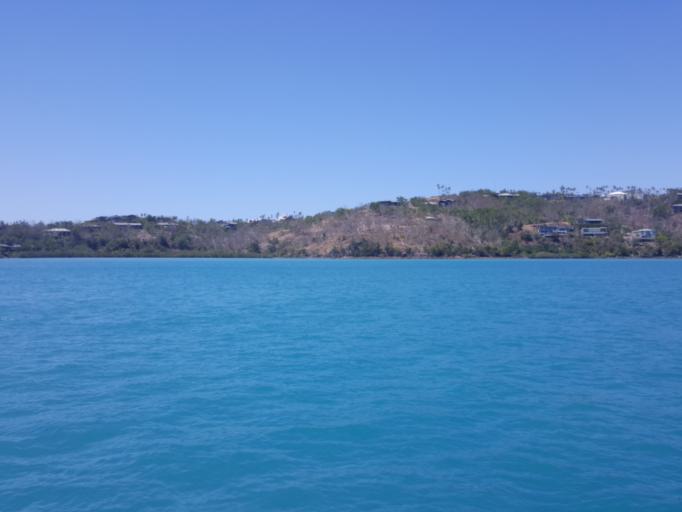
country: AU
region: Queensland
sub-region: Whitsunday
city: Proserpine
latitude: -20.3360
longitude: 148.9435
